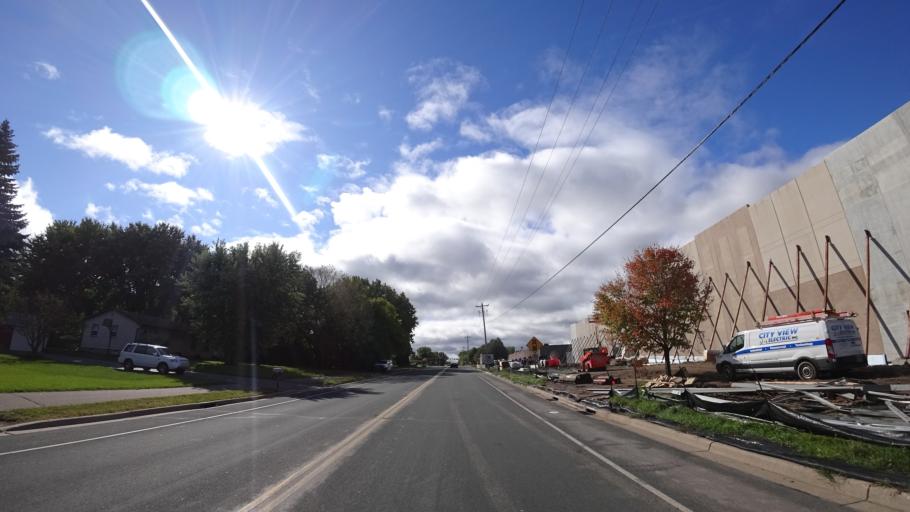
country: US
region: Minnesota
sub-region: Dakota County
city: Eagan
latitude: 44.8078
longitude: -93.2179
